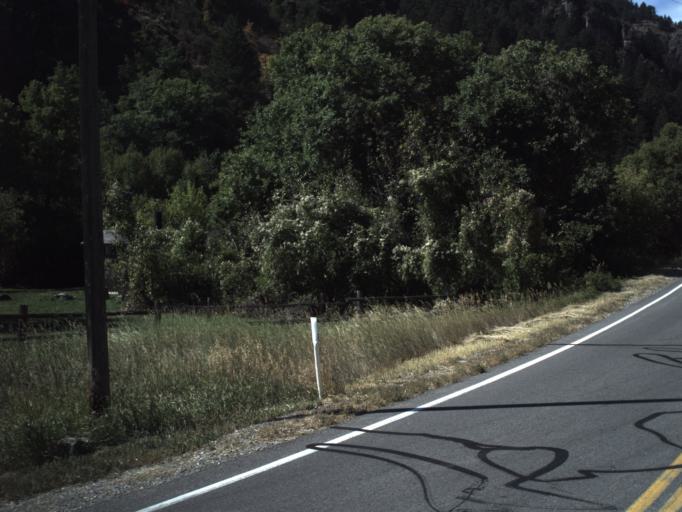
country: US
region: Utah
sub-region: Cache County
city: Millville
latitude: 41.6295
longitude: -111.6970
